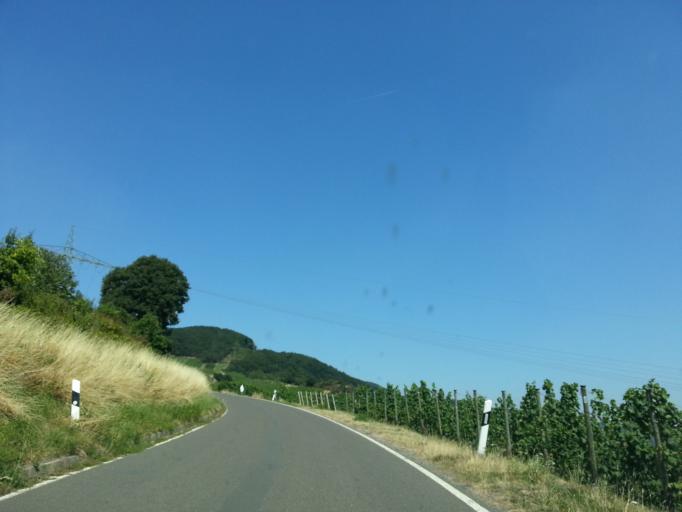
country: DE
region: Rheinland-Pfalz
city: Wintrich
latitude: 49.8778
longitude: 6.9434
